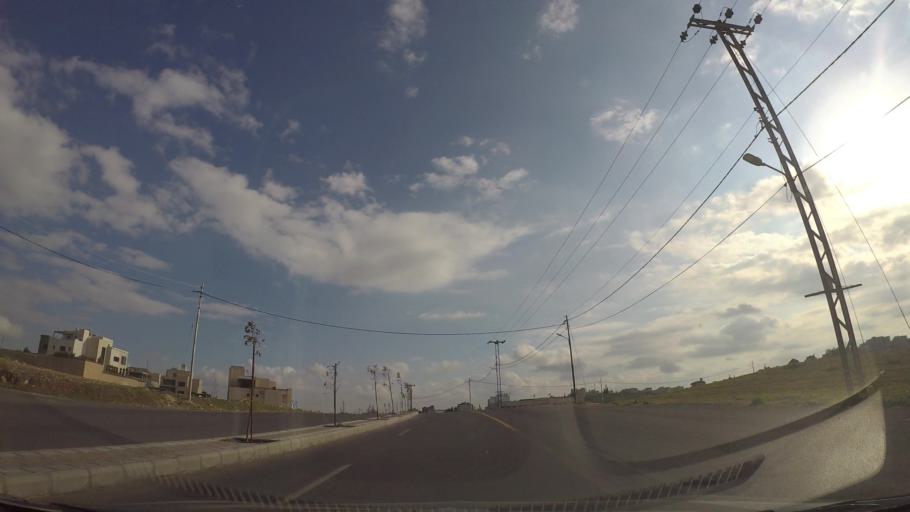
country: JO
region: Amman
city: Umm as Summaq
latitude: 31.9185
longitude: 35.8486
